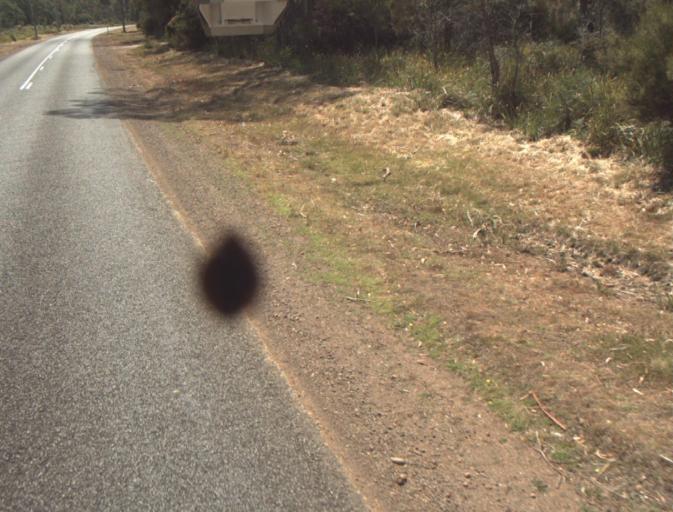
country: AU
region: Tasmania
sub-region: Launceston
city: Mayfield
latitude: -41.3108
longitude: 147.1341
